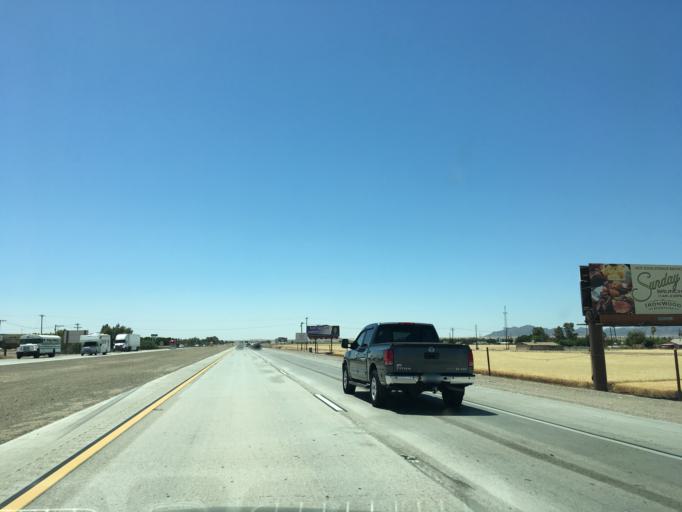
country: US
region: Arizona
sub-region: Yuma County
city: Yuma
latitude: 32.7331
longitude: -114.6300
